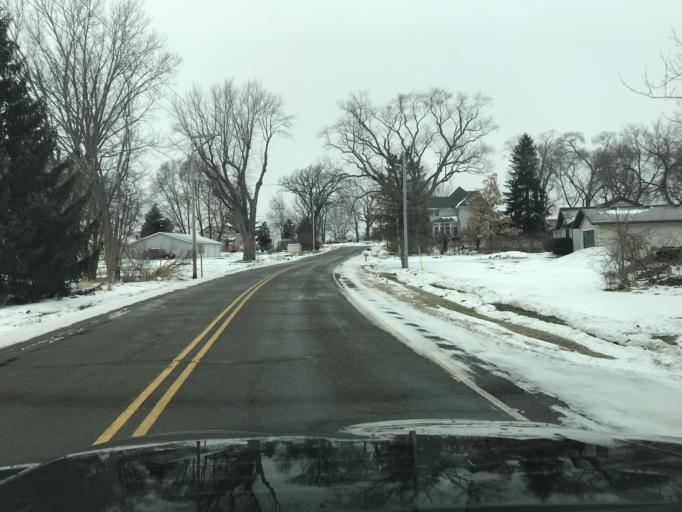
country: US
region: Wisconsin
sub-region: Dane County
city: Cottage Grove
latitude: 43.0884
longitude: -89.2342
